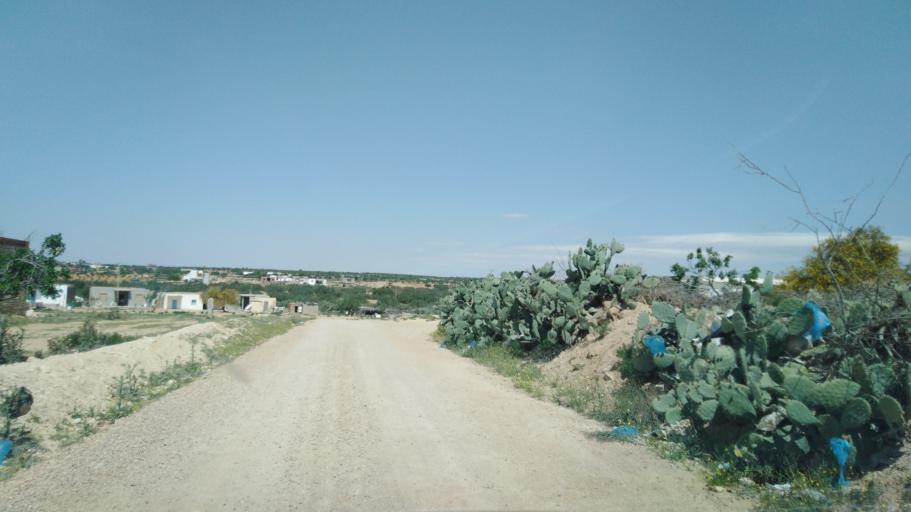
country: TN
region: Safaqis
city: Sfax
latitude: 34.7601
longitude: 10.5253
